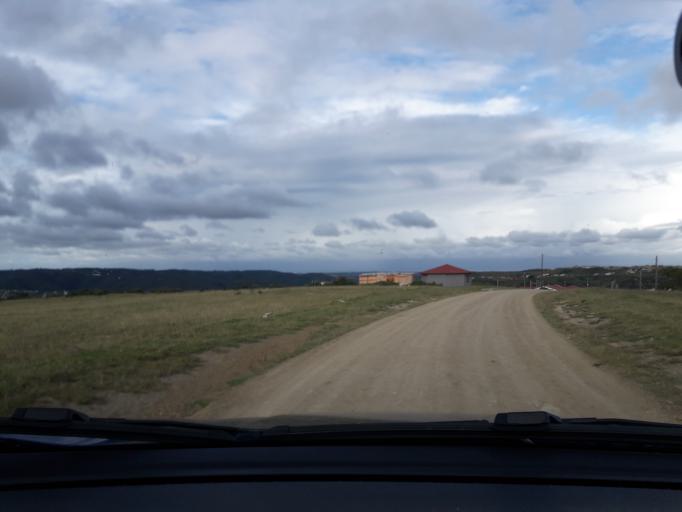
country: ZA
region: Eastern Cape
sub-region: Buffalo City Metropolitan Municipality
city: East London
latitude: -32.8041
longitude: 27.9539
